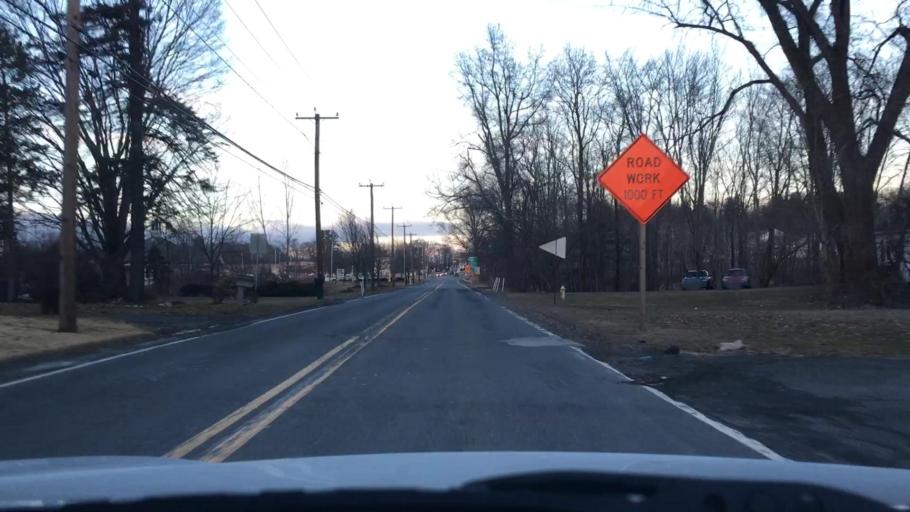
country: US
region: Massachusetts
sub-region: Hampden County
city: Southwick
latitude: 42.0228
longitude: -72.7876
